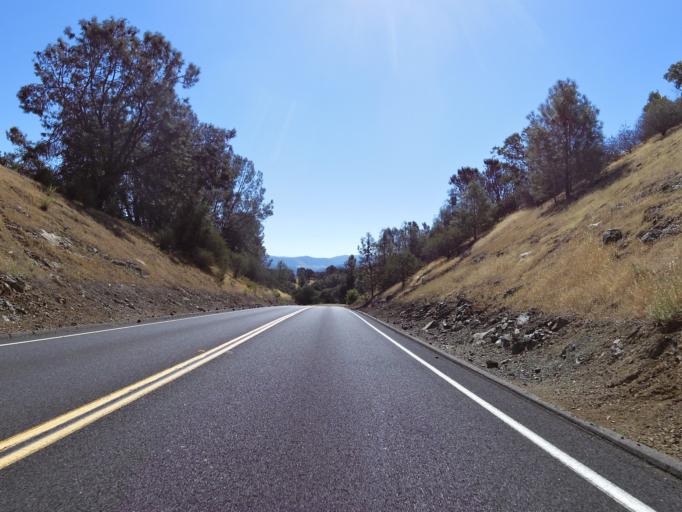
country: US
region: California
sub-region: Tuolumne County
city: Tuolumne City
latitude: 37.6997
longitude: -120.2860
